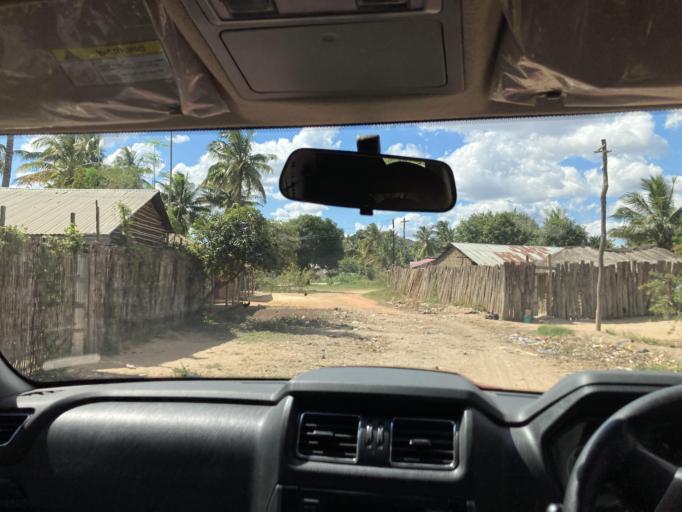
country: MZ
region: Cabo Delgado
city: Montepuez
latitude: -13.1364
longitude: 39.0029
